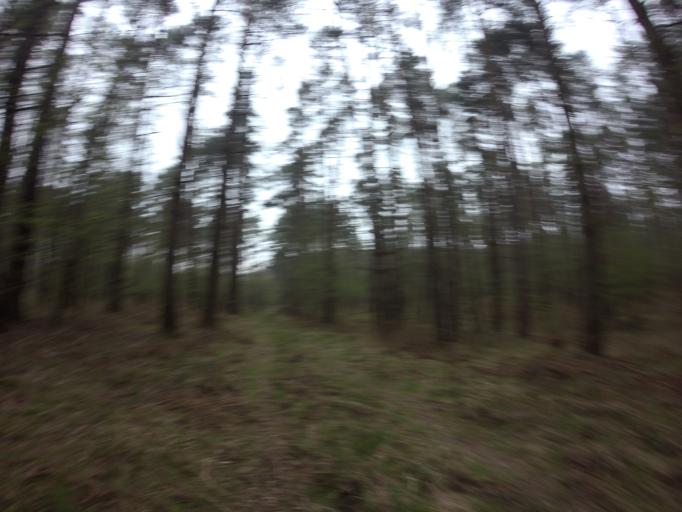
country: PL
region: West Pomeranian Voivodeship
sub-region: Powiat choszczenski
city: Recz
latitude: 53.1891
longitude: 15.5362
